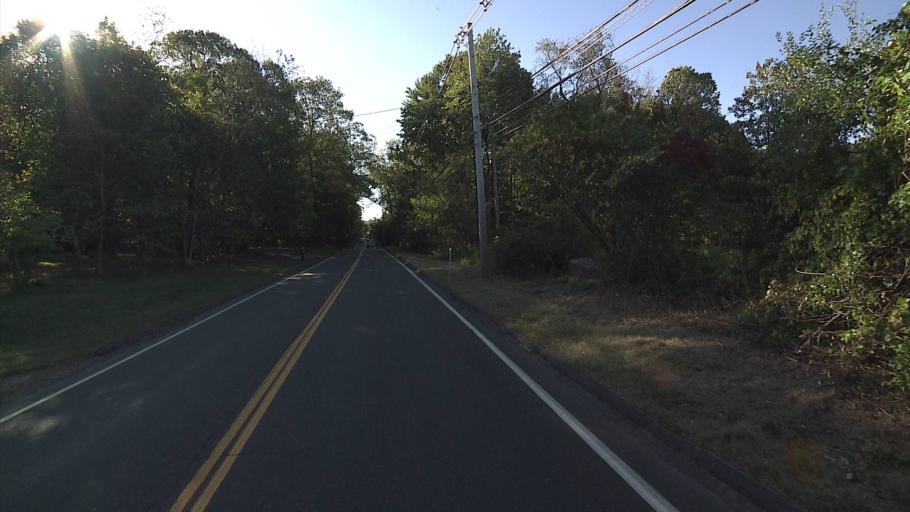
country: US
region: Connecticut
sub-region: New Haven County
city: Wallingford Center
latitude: 41.4745
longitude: -72.7629
